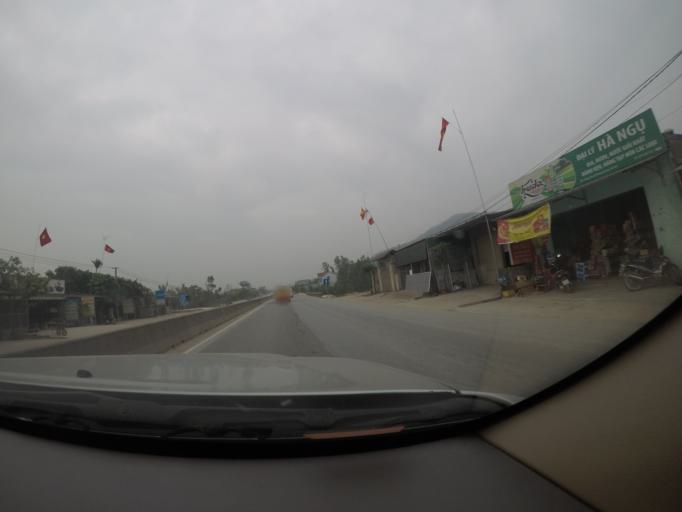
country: VN
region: Ha Tinh
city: Ky Anh
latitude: 18.1409
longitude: 106.2509
